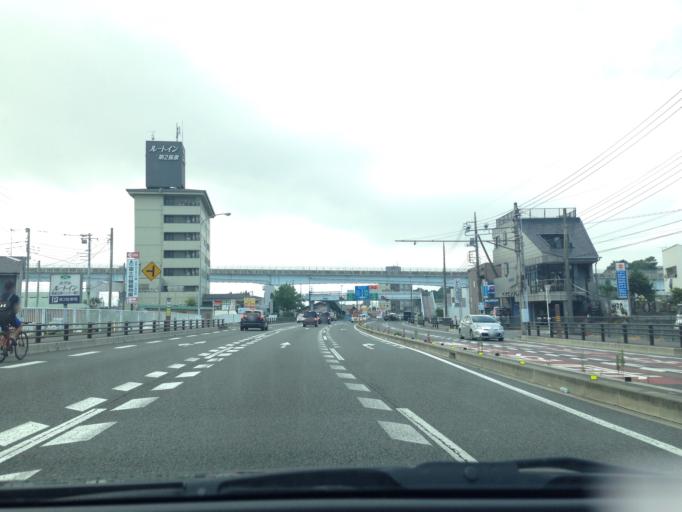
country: JP
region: Shizuoka
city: Mishima
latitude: 35.1524
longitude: 138.8948
